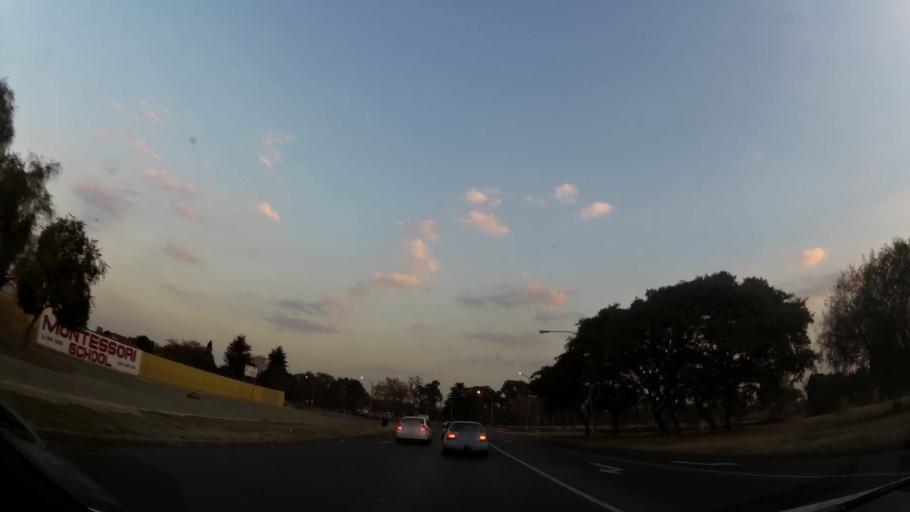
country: ZA
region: Gauteng
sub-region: Ekurhuleni Metropolitan Municipality
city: Springs
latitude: -26.2658
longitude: 28.4275
